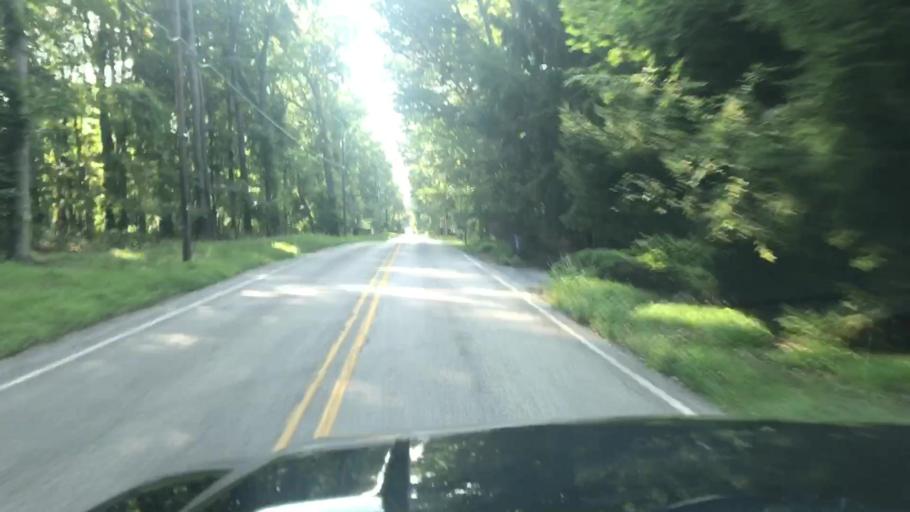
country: US
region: Pennsylvania
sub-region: York County
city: Valley Green
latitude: 40.1545
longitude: -76.8465
